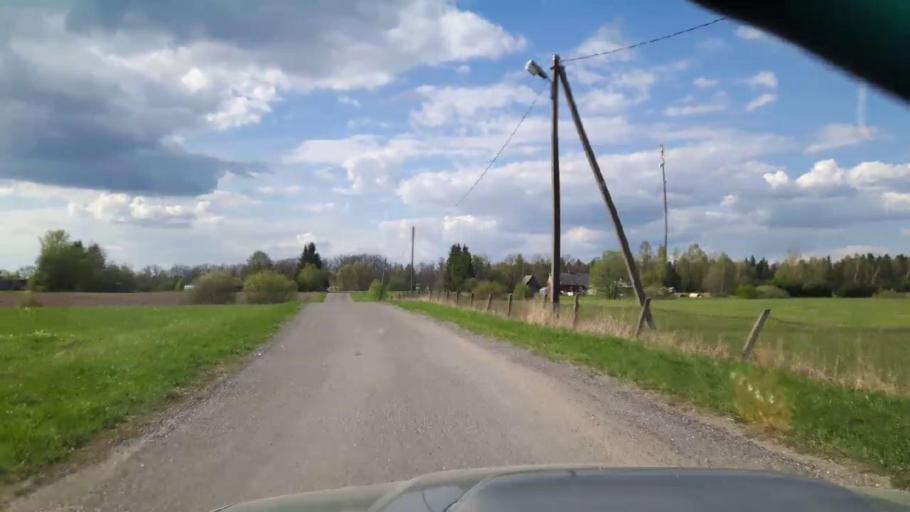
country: EE
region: Paernumaa
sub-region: Sindi linn
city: Sindi
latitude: 58.4465
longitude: 24.7692
